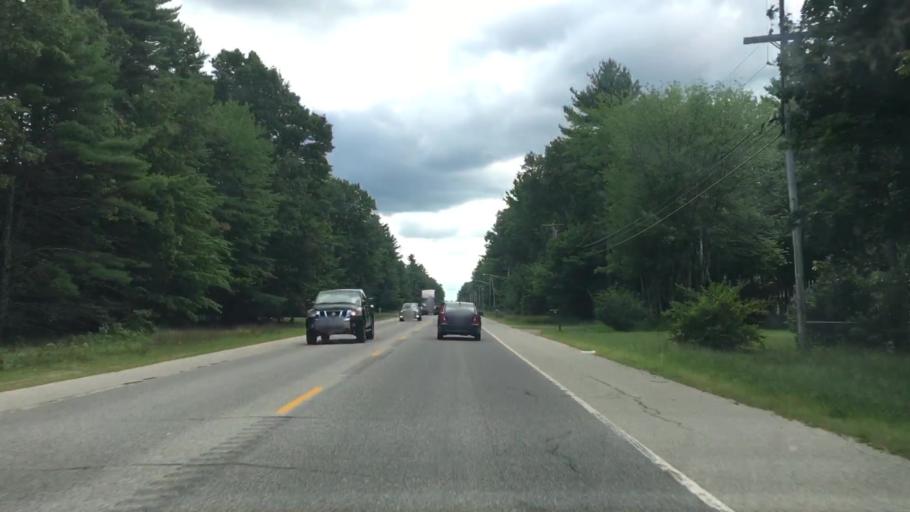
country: US
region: Maine
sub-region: York County
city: North Berwick
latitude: 43.3370
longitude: -70.7334
